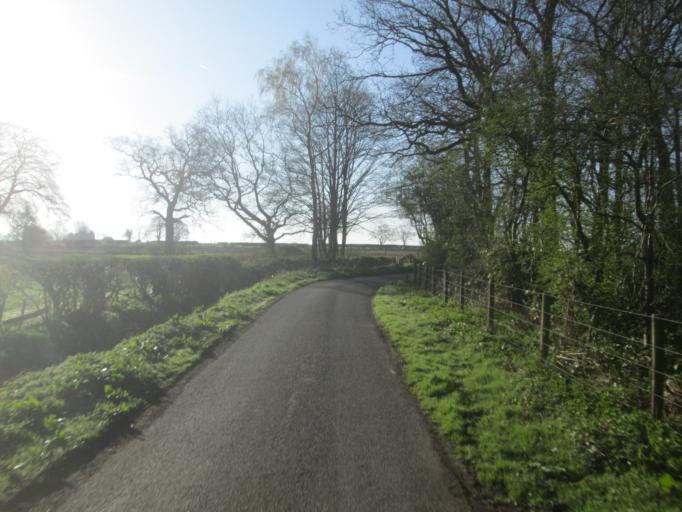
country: GB
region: England
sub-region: Derbyshire
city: Duffield
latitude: 52.9781
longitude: -1.5208
